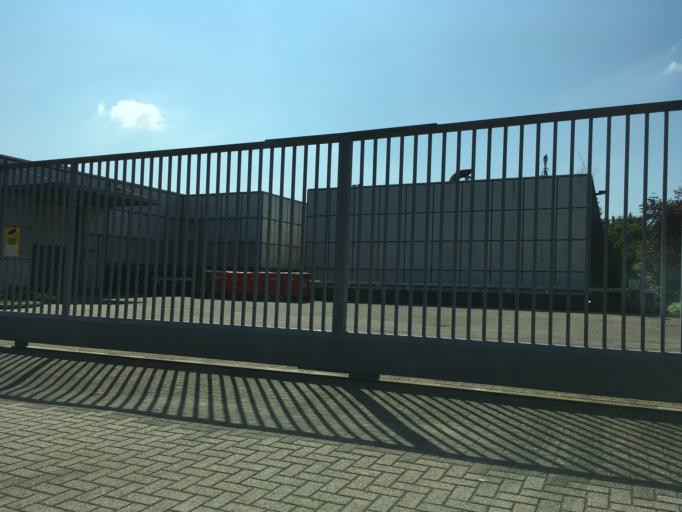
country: GB
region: England
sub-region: South Gloucestershire
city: Almondsbury
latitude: 51.5409
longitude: -2.5826
